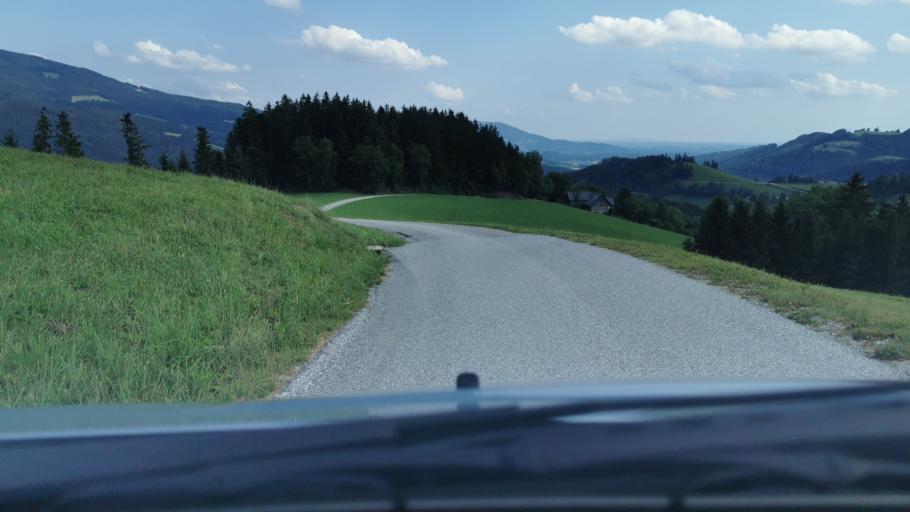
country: AT
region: Styria
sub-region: Politischer Bezirk Weiz
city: Koglhof
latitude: 47.3208
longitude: 15.6691
